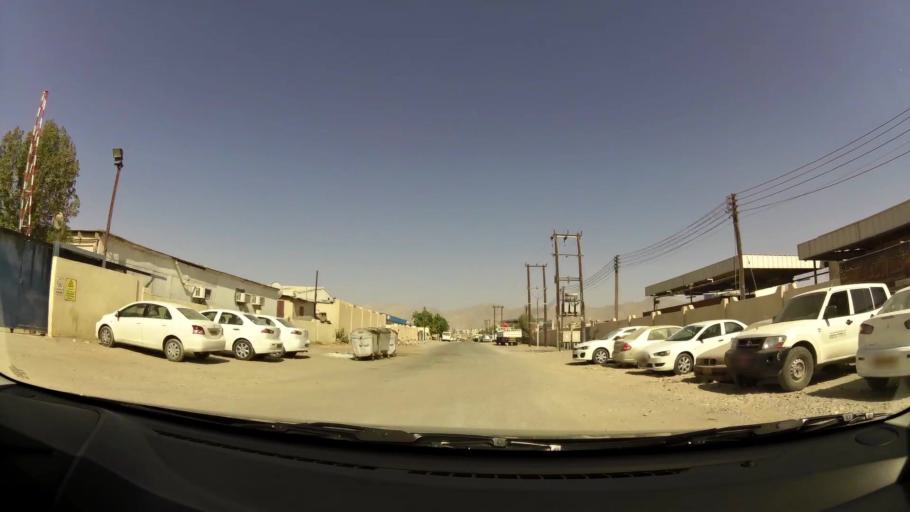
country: OM
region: Muhafazat Masqat
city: Bawshar
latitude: 23.5674
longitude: 58.3517
